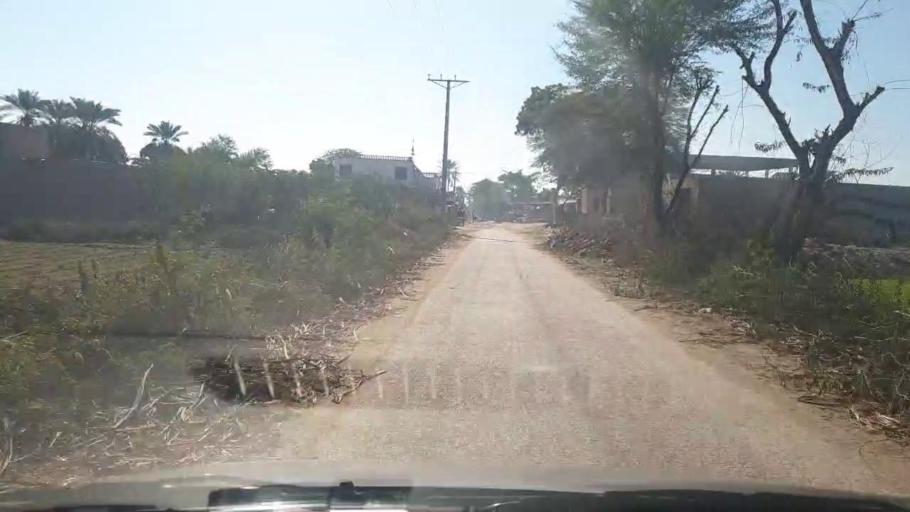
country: PK
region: Sindh
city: Bozdar
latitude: 27.2466
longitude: 68.6521
